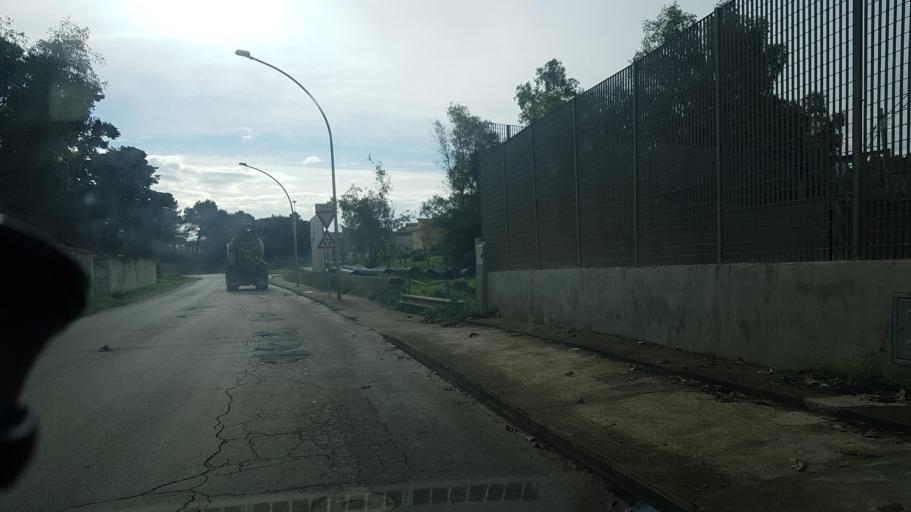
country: IT
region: Apulia
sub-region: Provincia di Brindisi
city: San Vito dei Normanni
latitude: 40.6638
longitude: 17.7054
